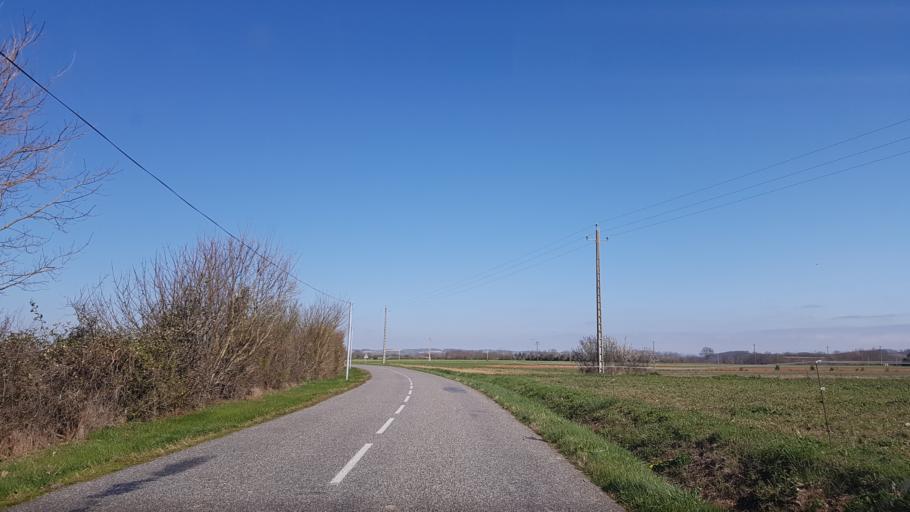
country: FR
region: Languedoc-Roussillon
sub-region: Departement de l'Aude
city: Belpech
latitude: 43.1569
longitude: 1.7079
